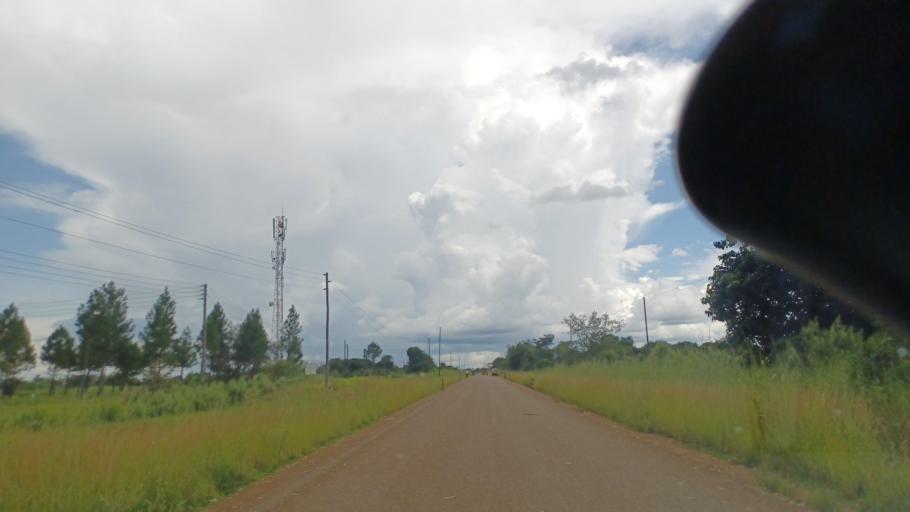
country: ZM
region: North-Western
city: Kasempa
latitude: -13.1071
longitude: 25.8703
